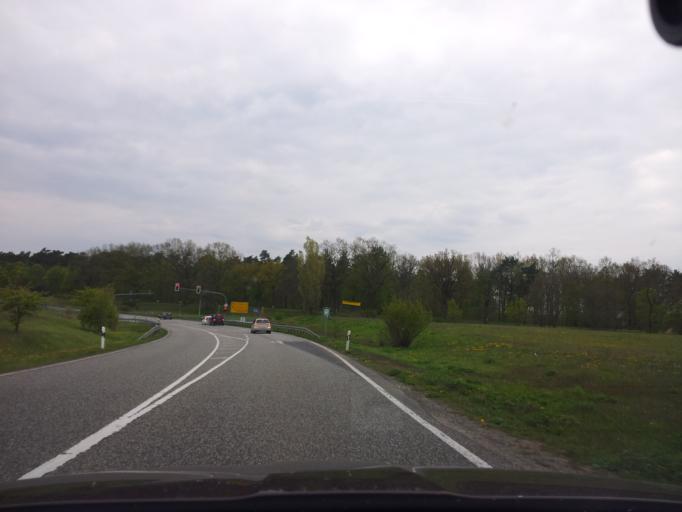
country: DE
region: Brandenburg
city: Muncheberg
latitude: 52.4983
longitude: 14.1090
